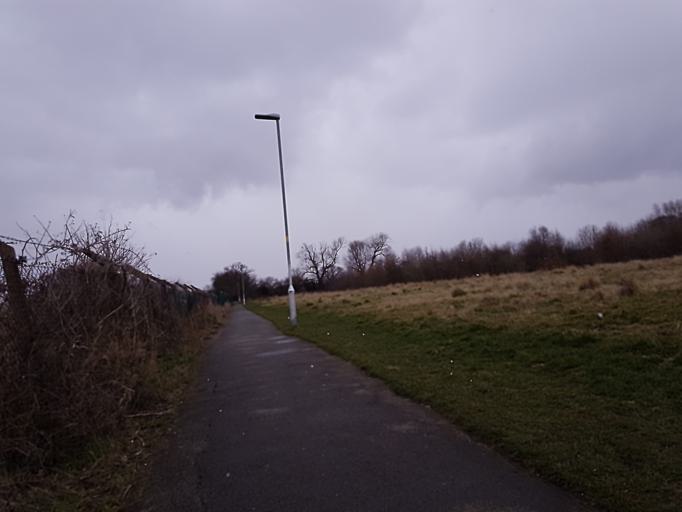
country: GB
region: England
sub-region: North East Lincolnshire
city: Grimbsy
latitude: 53.5577
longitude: -0.1032
